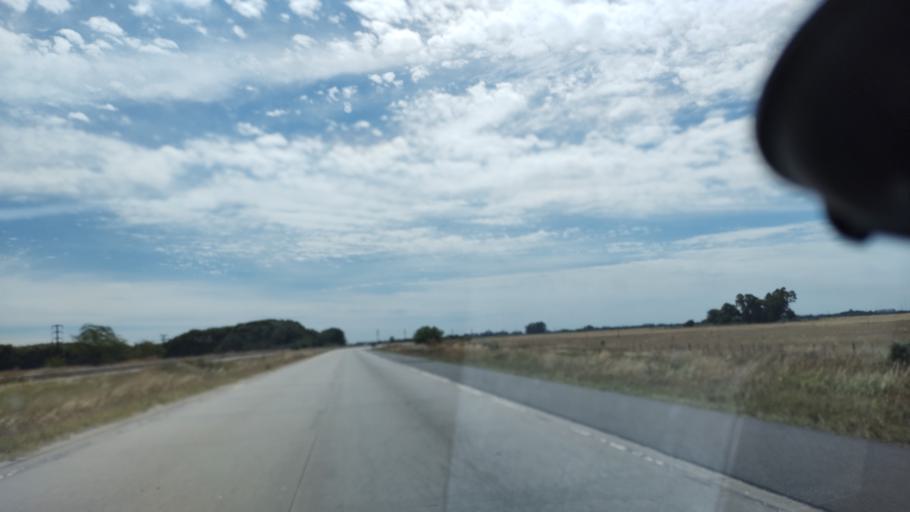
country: AR
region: Buenos Aires
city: Canuelas
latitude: -35.0763
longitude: -58.6856
